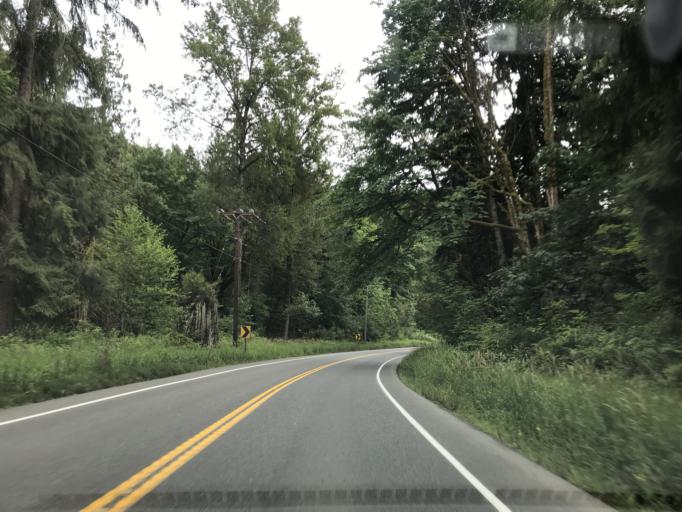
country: US
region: Washington
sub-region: King County
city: Fall City
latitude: 47.5491
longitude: -121.8994
